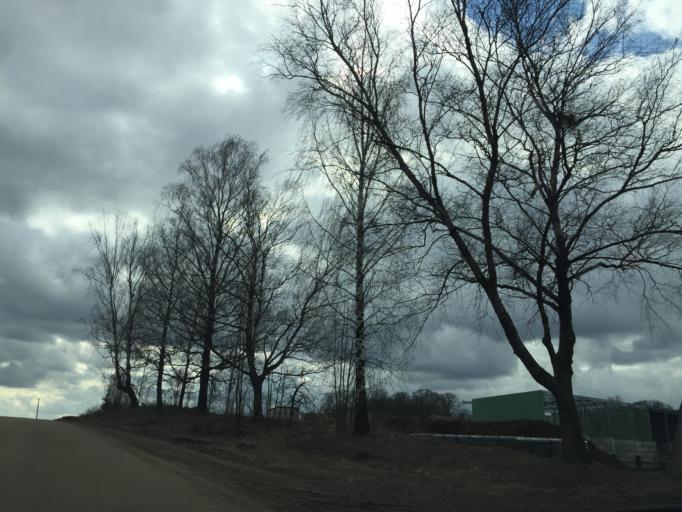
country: LV
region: Vecumnieki
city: Vecumnieki
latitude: 56.5041
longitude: 24.7166
